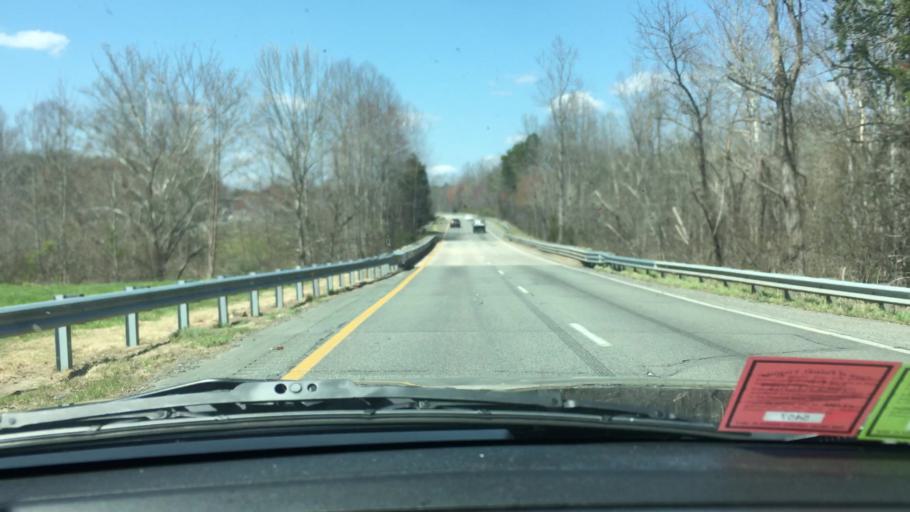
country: US
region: North Carolina
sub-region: Surry County
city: Pilot Mountain
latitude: 36.3966
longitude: -80.4915
